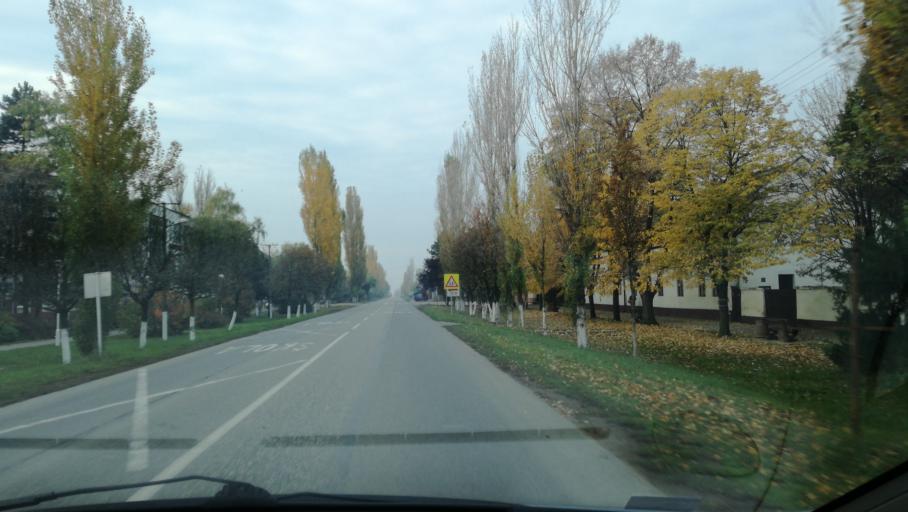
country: RS
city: Basaid
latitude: 45.6423
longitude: 20.4149
